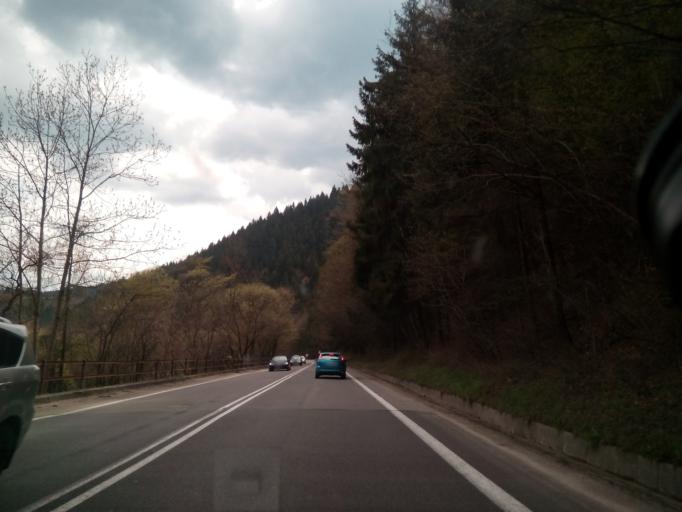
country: SK
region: Zilinsky
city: Ruzomberok
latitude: 49.1136
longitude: 19.2244
